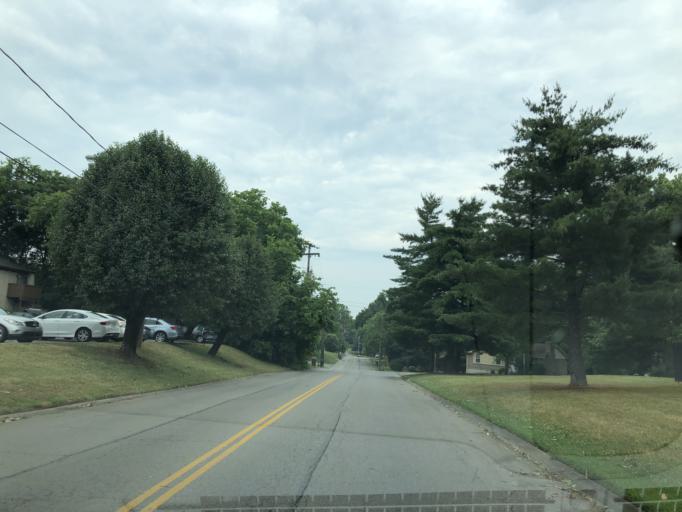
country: US
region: Tennessee
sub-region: Davidson County
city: Oak Hill
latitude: 36.0733
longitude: -86.6895
